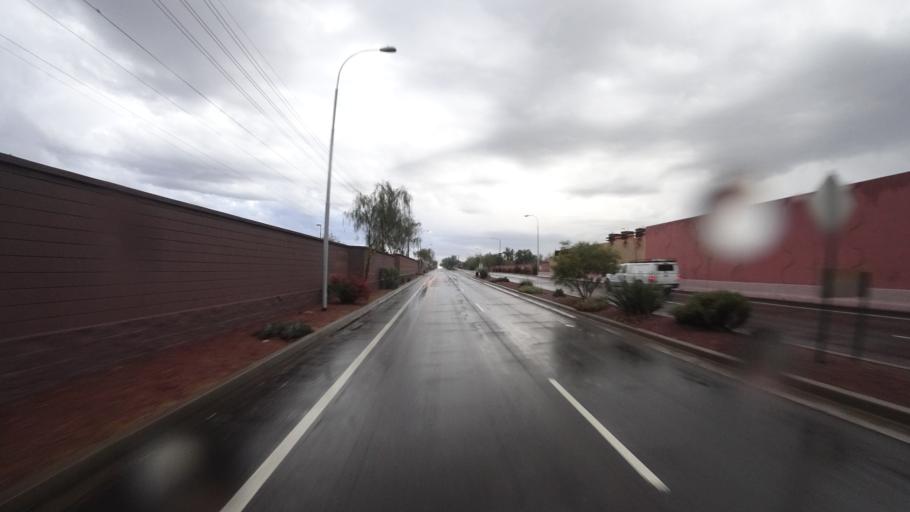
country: US
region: Arizona
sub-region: Maricopa County
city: Paradise Valley
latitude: 33.4776
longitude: -111.9434
